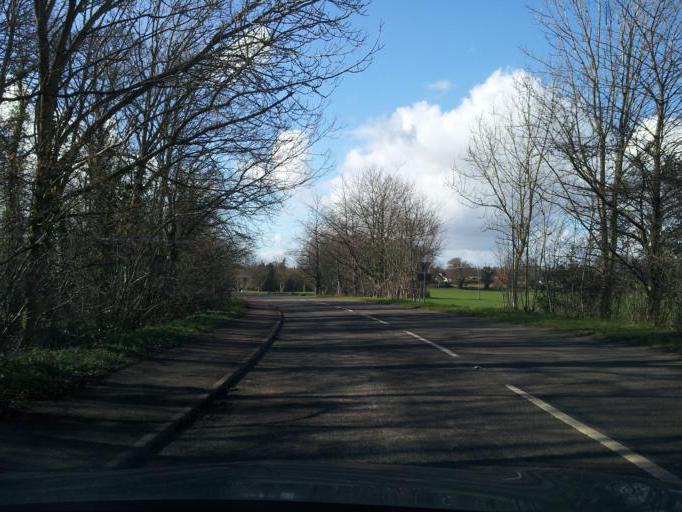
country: GB
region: England
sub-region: Norfolk
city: Brundall
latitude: 52.6392
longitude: 1.4490
